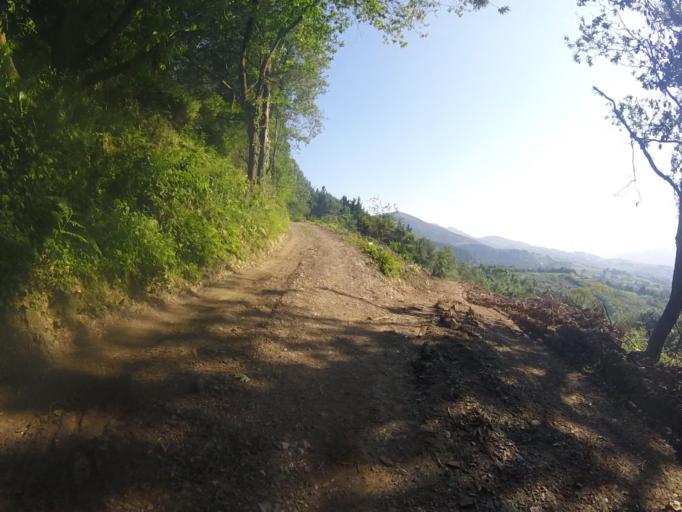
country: ES
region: Basque Country
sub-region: Provincia de Guipuzcoa
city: Astigarraga
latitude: 43.2620
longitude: -1.9360
